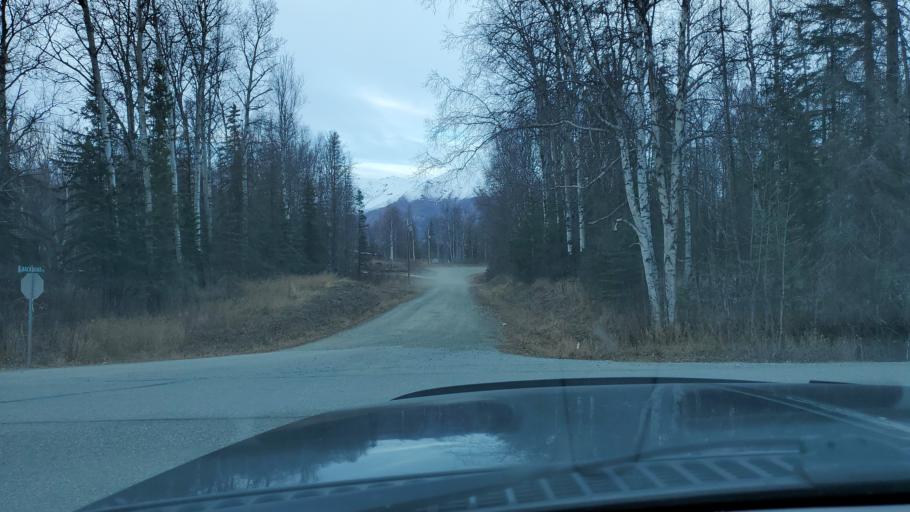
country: US
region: Alaska
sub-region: Matanuska-Susitna Borough
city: Lakes
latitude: 61.6572
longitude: -149.3036
